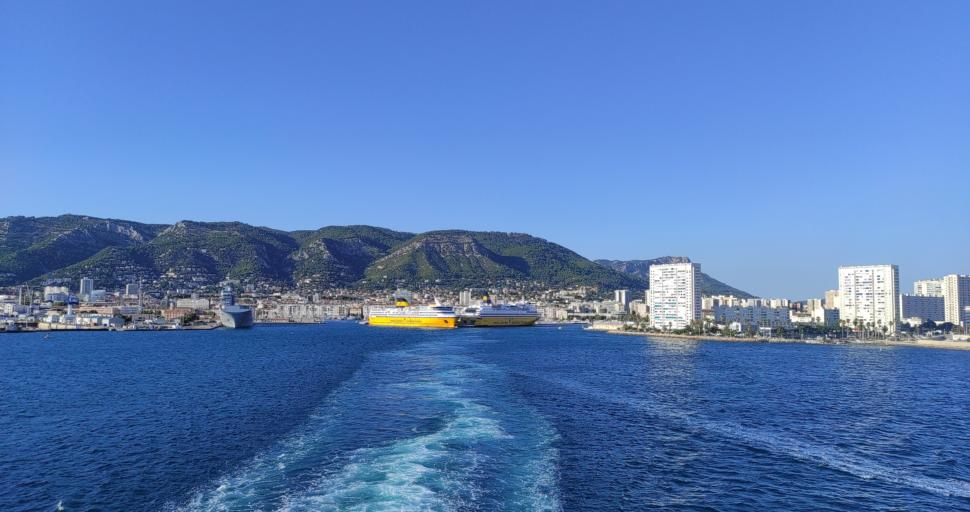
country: FR
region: Provence-Alpes-Cote d'Azur
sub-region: Departement du Var
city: Toulon
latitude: 43.1097
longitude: 5.9242
